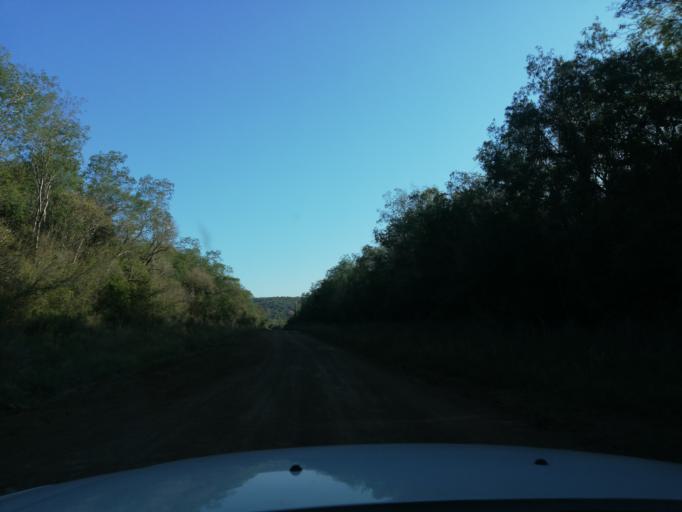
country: AR
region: Misiones
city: Cerro Cora
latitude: -27.6031
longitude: -55.7010
